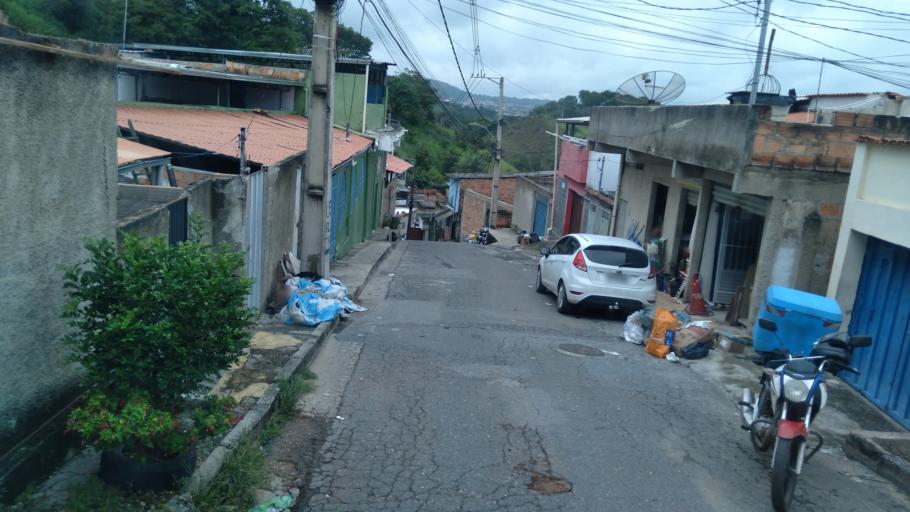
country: BR
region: Minas Gerais
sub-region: Santa Luzia
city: Santa Luzia
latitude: -19.8282
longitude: -43.8679
